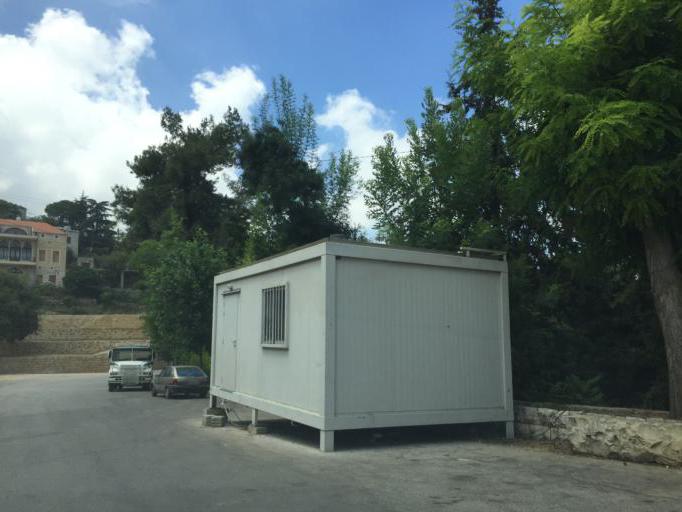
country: LB
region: Mont-Liban
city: Beit ed Dine
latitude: 33.6939
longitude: 35.5797
